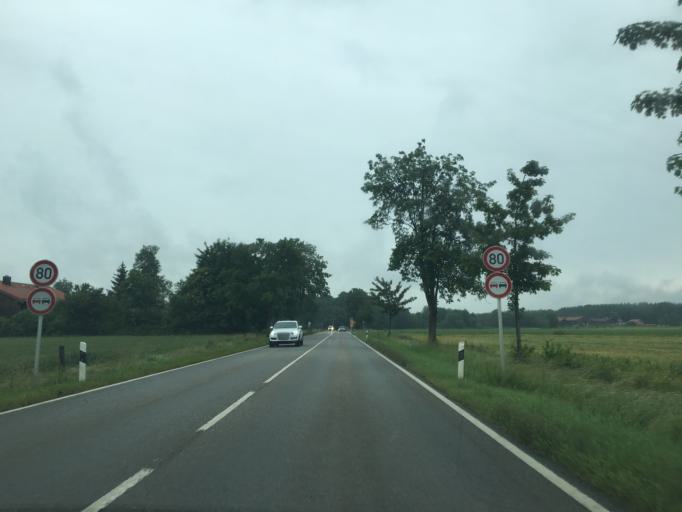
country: DE
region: Bavaria
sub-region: Upper Bavaria
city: Holzkirchen
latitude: 47.8704
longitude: 11.7181
